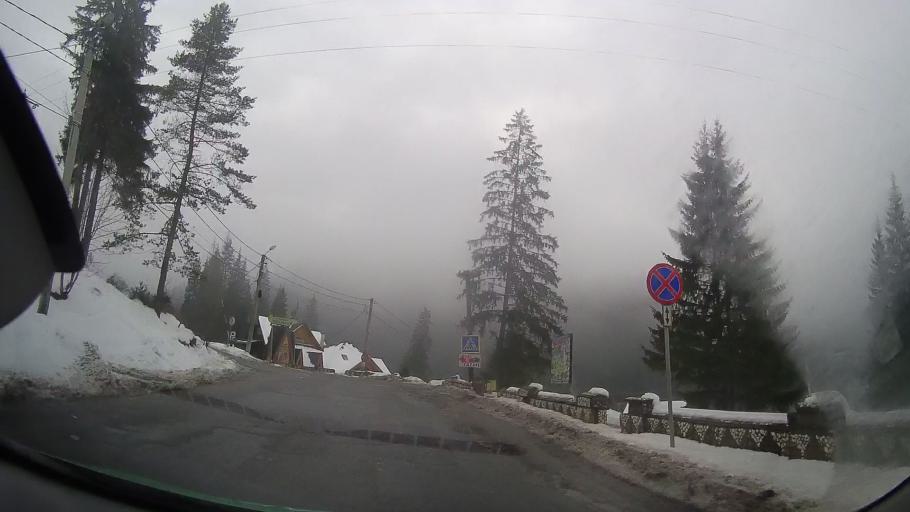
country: RO
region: Neamt
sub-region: Comuna Bicaz Chei
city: Bicaz Chei
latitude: 46.7909
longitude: 25.7897
